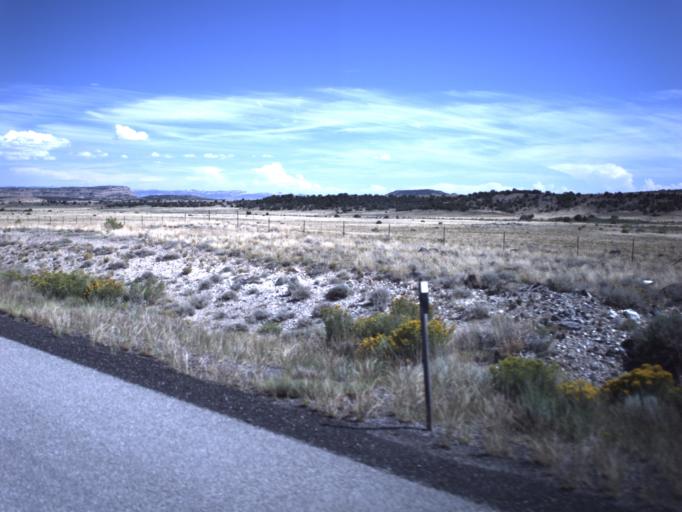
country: US
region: Utah
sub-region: Emery County
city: Ferron
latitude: 38.7714
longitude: -111.3330
